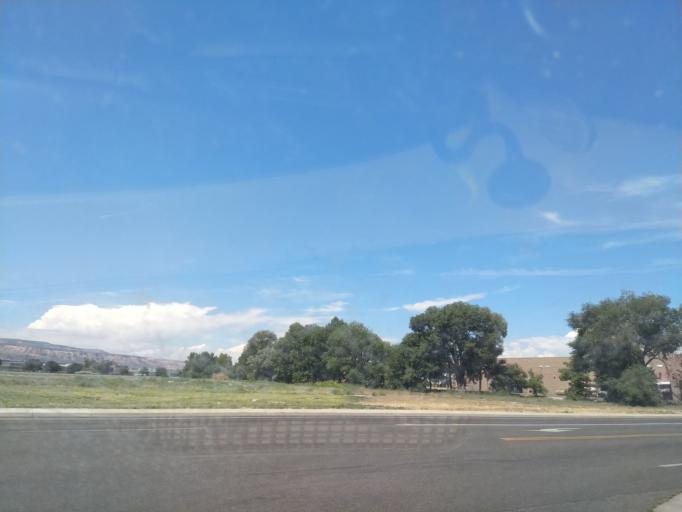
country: US
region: Colorado
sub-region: Mesa County
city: Grand Junction
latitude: 39.0748
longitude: -108.5801
